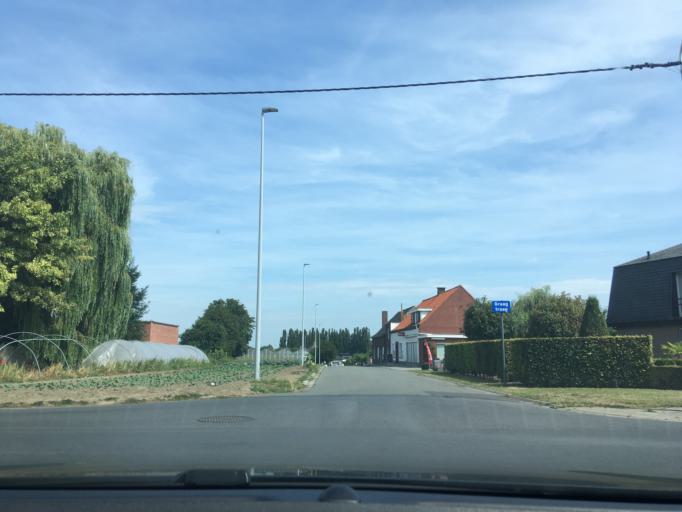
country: BE
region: Flanders
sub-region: Provincie West-Vlaanderen
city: Ledegem
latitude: 50.8916
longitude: 3.1176
